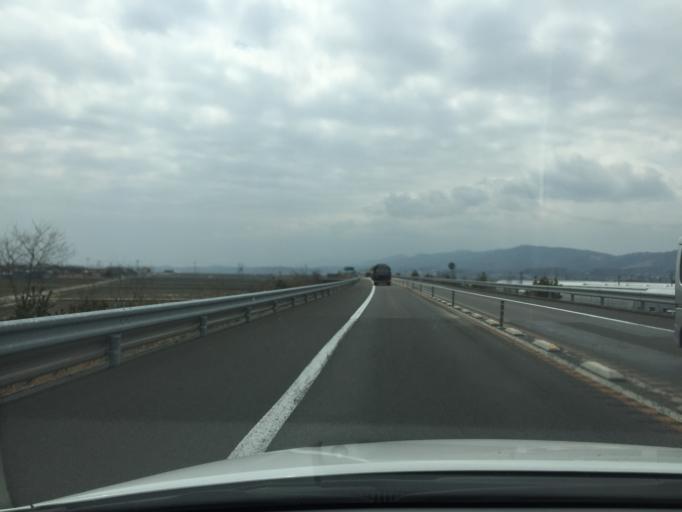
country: JP
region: Miyagi
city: Watari
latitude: 38.0071
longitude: 140.8813
